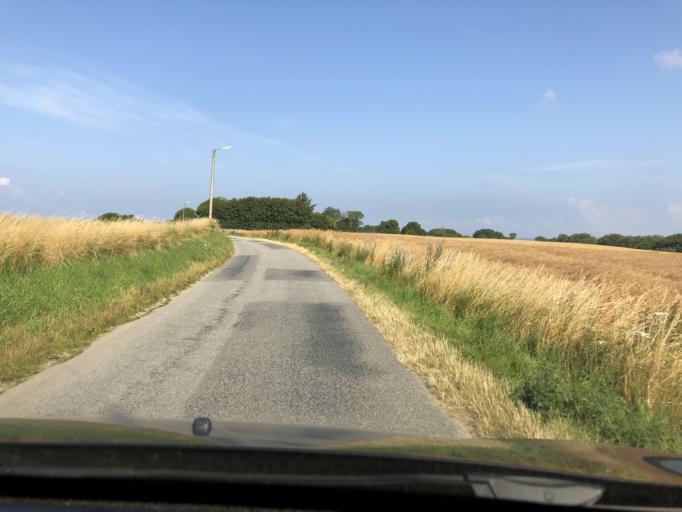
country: DK
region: South Denmark
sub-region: Faaborg-Midtfyn Kommune
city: Faaborg
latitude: 54.9477
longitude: 10.2355
